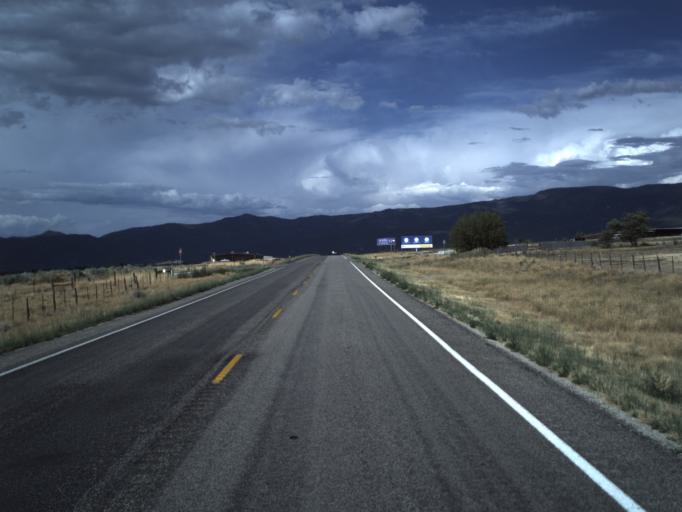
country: US
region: Utah
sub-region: Sanpete County
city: Mount Pleasant
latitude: 39.5202
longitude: -111.4818
